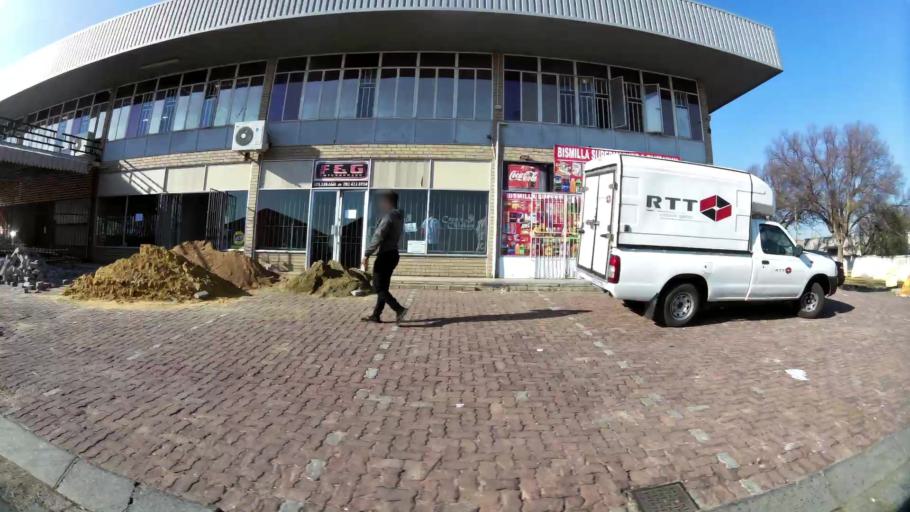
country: ZA
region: Gauteng
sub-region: City of Johannesburg Metropolitan Municipality
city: Modderfontein
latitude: -26.1330
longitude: 28.1467
